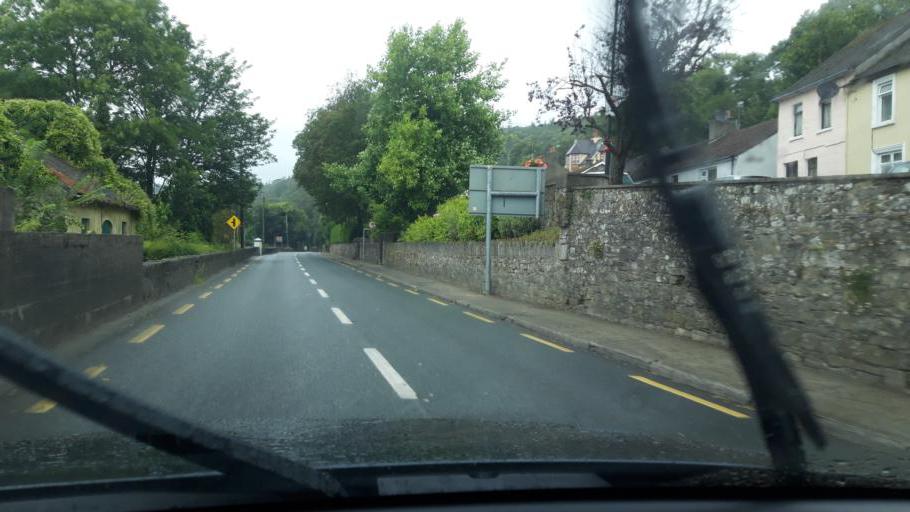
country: IE
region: Munster
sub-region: County Cork
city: Youghal
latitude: 52.1481
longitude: -7.8531
